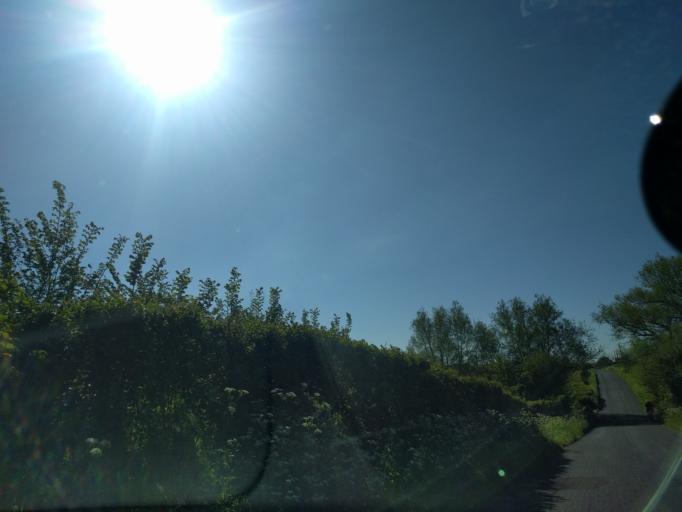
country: GB
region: England
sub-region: Wiltshire
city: Bratton
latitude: 51.2955
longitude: -2.1334
